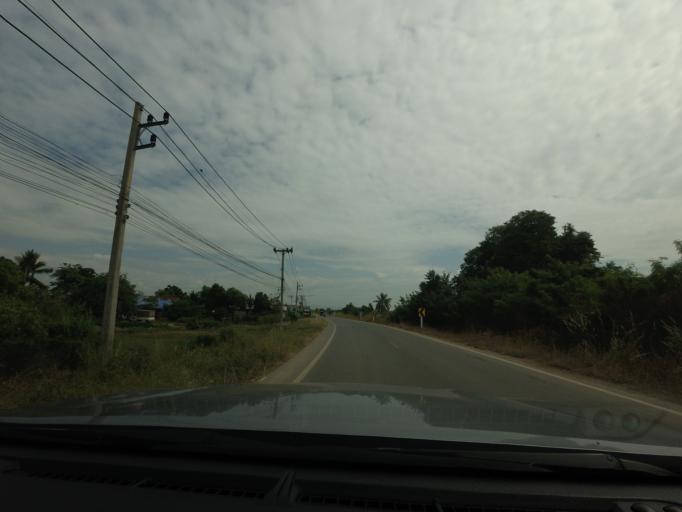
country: TH
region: Phitsanulok
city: Phitsanulok
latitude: 16.7194
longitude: 100.3281
